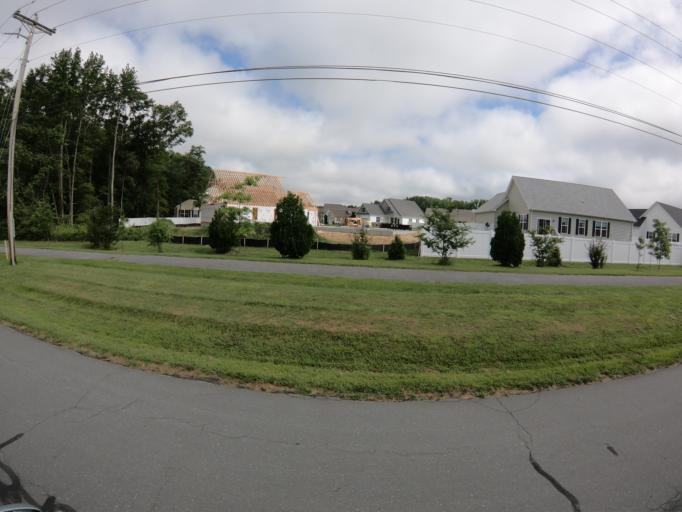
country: US
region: Delaware
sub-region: Kent County
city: Riverview
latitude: 39.0104
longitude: -75.4980
